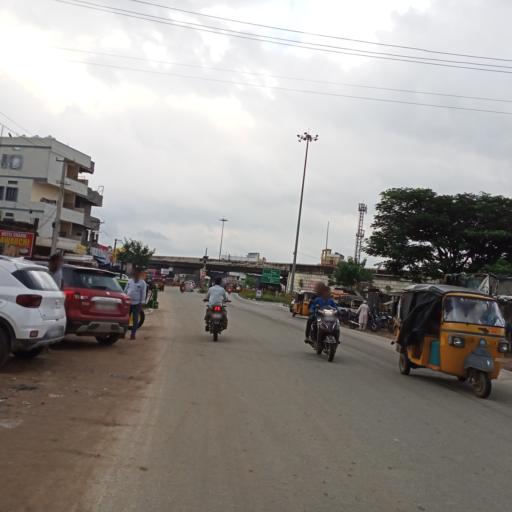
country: IN
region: Telangana
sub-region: Mahbubnagar
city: Mahbubnagar
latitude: 16.7742
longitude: 78.1305
